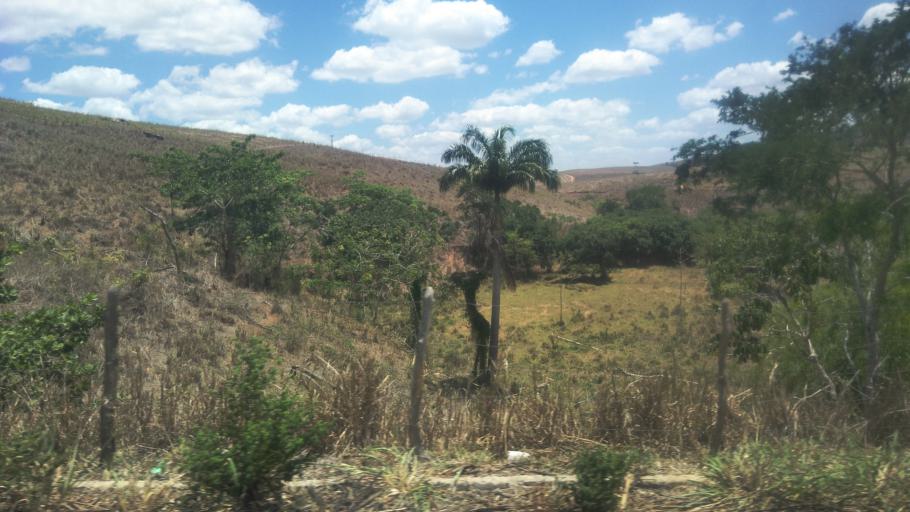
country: BR
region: Pernambuco
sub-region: Nazare Da Mata
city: Nazare da Mata
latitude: -7.7384
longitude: -35.2915
